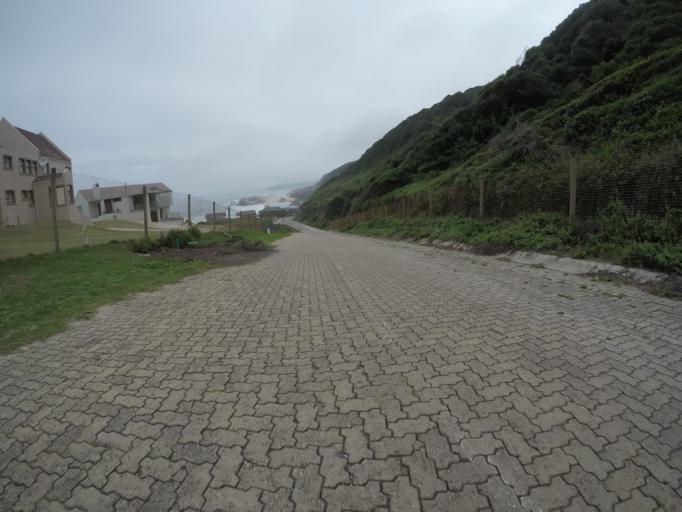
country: ZA
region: Eastern Cape
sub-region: Cacadu District Municipality
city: Kareedouw
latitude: -34.0742
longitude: 24.2293
